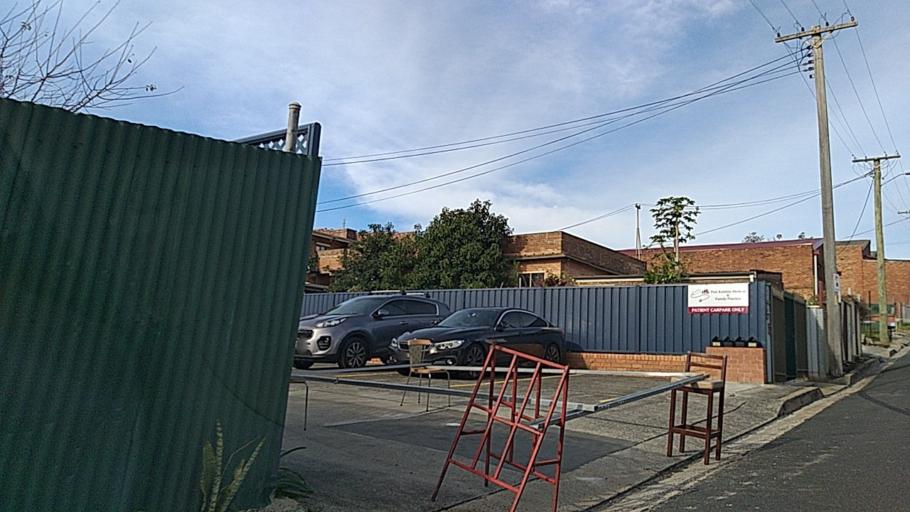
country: AU
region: New South Wales
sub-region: Wollongong
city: Port Kembla
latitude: -34.4823
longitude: 150.9021
